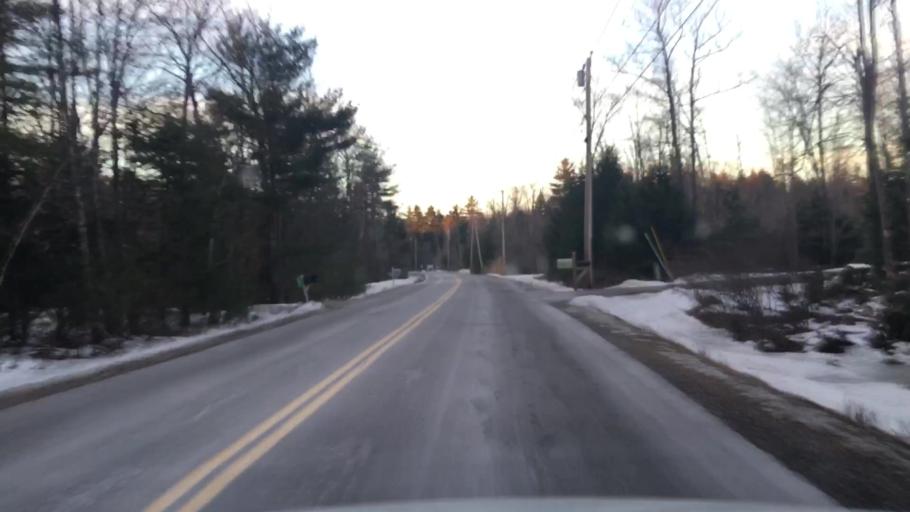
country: US
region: Maine
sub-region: York County
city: Lebanon
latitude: 43.3541
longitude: -70.8685
